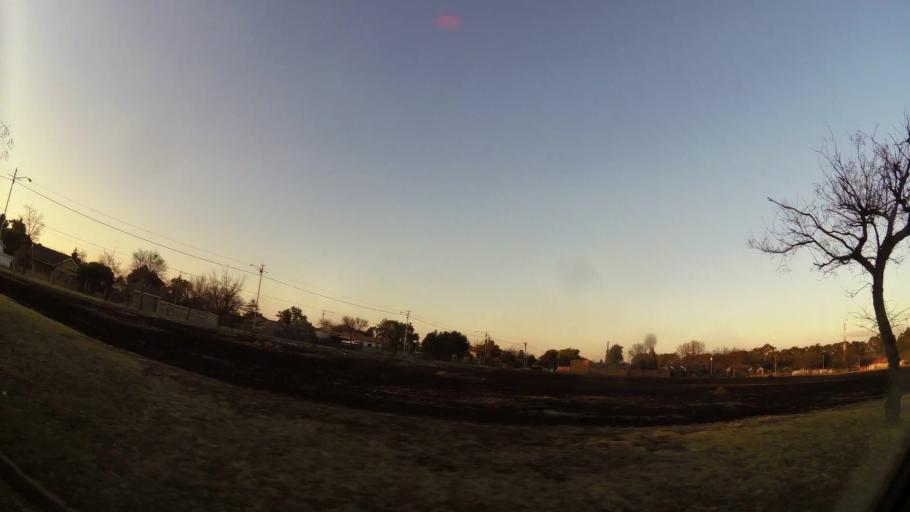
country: ZA
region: Gauteng
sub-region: Ekurhuleni Metropolitan Municipality
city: Germiston
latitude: -26.2751
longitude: 28.1518
